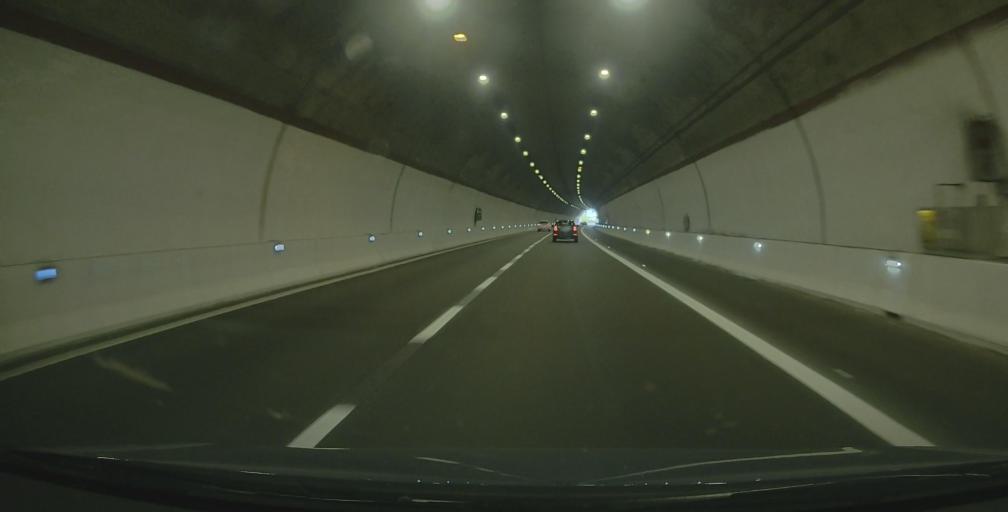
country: IT
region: Calabria
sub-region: Provincia di Vibo-Valentia
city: Francica
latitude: 38.5756
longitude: 16.1151
